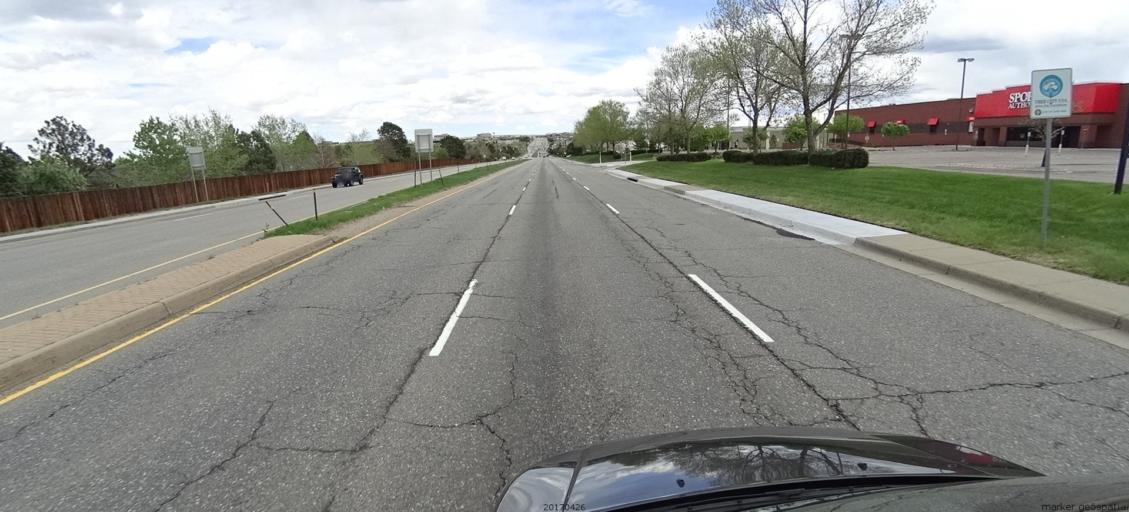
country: US
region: Colorado
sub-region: Douglas County
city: Acres Green
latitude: 39.5659
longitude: -104.9008
